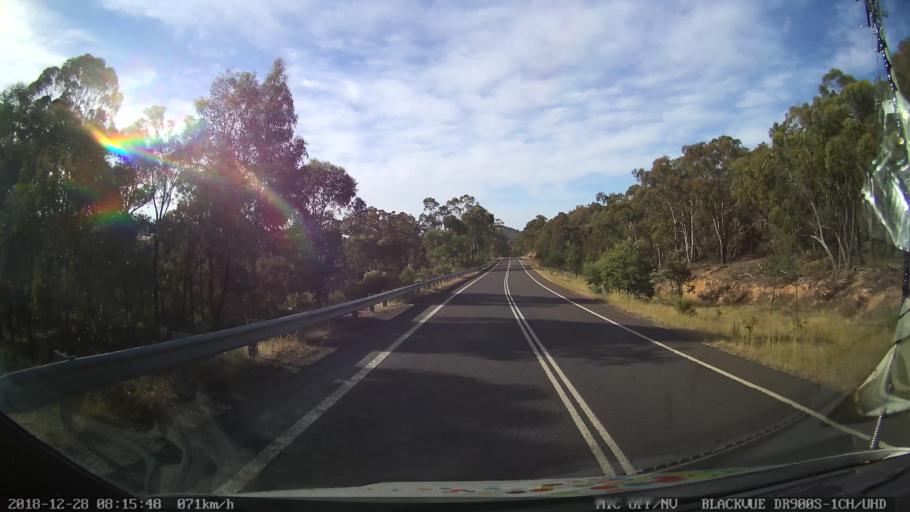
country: AU
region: New South Wales
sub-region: Blayney
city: Blayney
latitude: -33.8261
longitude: 149.3296
